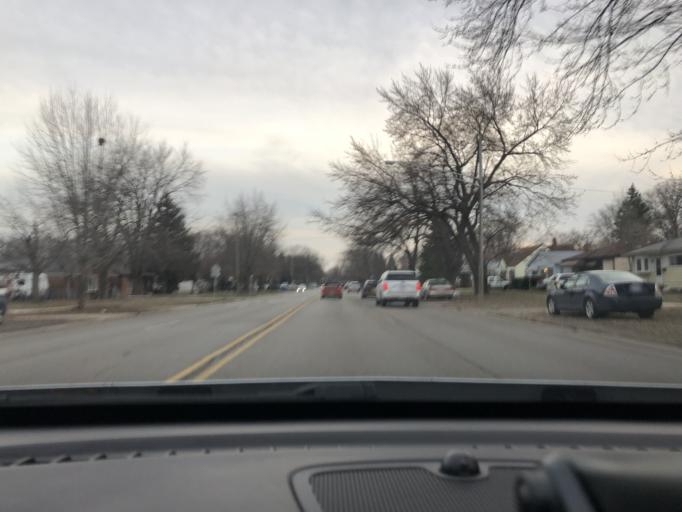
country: US
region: Michigan
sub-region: Wayne County
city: Allen Park
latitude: 42.2764
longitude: -83.2314
